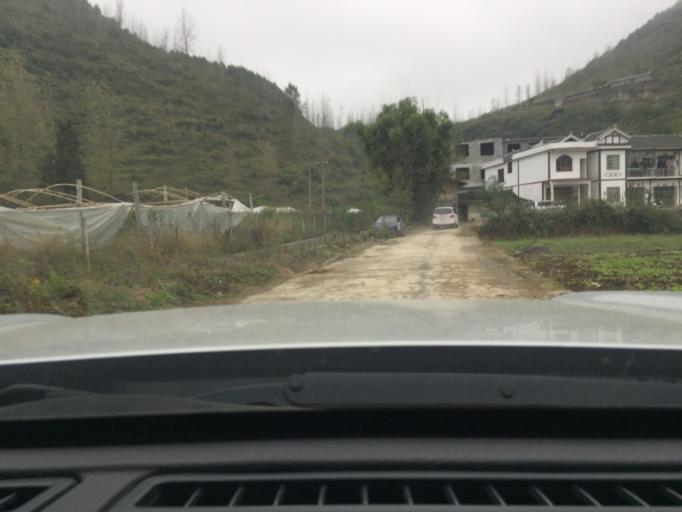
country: CN
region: Guizhou Sheng
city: Jiancha
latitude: 28.1696
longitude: 108.0049
